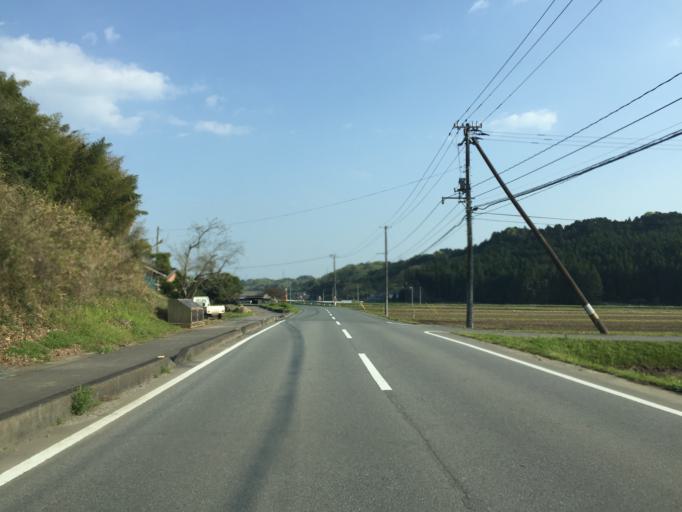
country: JP
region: Fukushima
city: Iwaki
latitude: 36.9711
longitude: 140.8024
